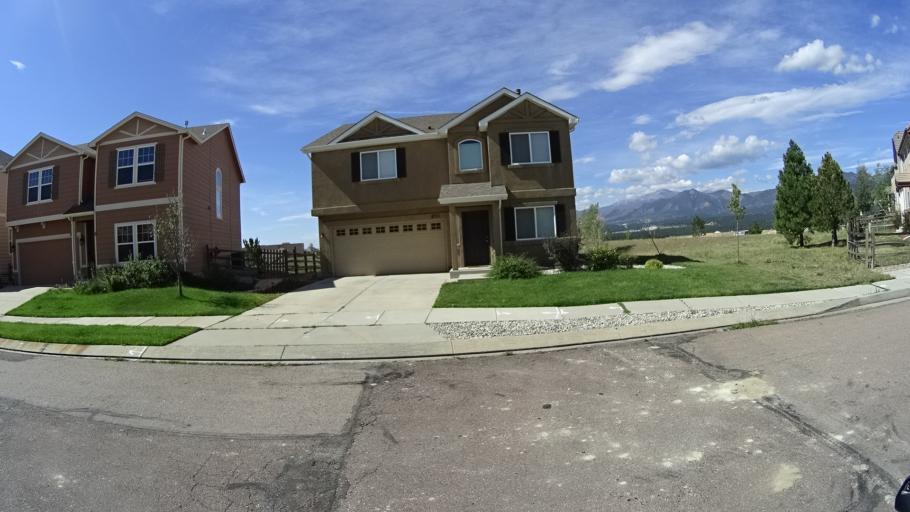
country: US
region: Colorado
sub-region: El Paso County
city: Gleneagle
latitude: 39.0240
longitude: -104.8126
